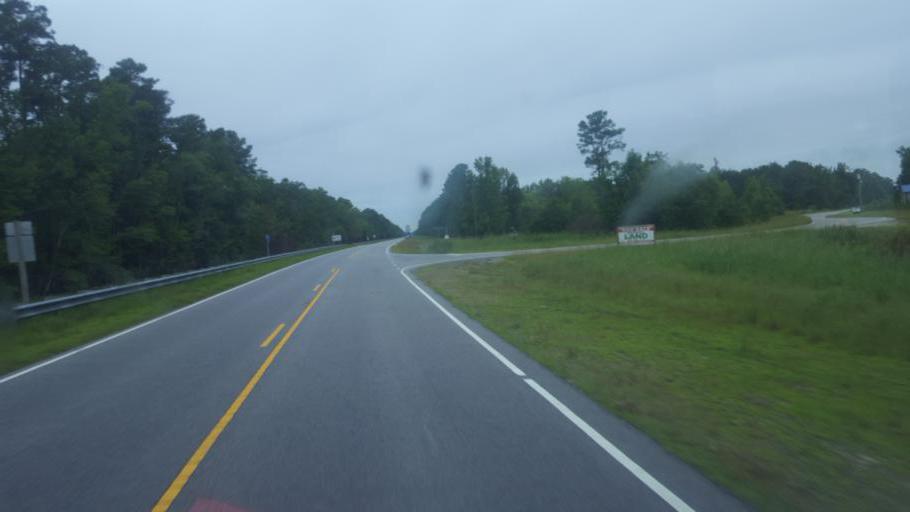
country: US
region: North Carolina
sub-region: Tyrrell County
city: Columbia
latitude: 35.9096
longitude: -76.1105
